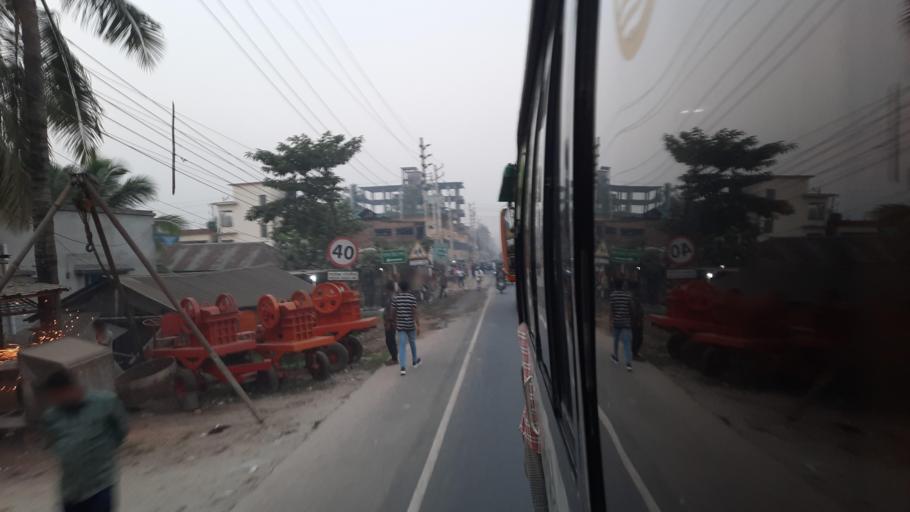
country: BD
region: Khulna
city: Jessore
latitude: 23.1707
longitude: 89.1927
